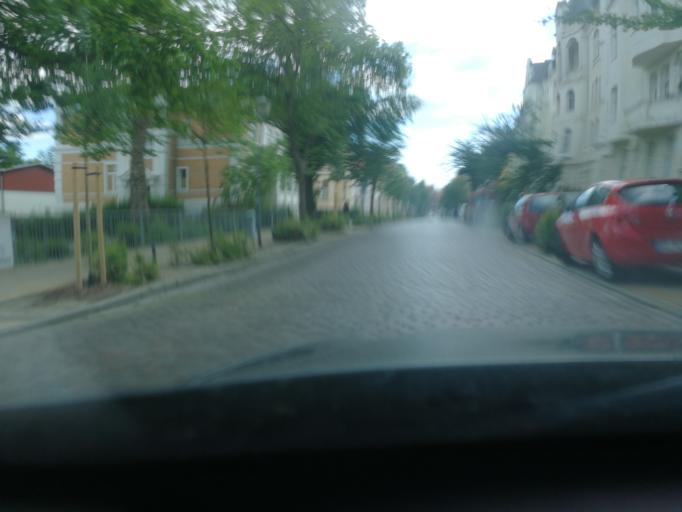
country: DE
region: Mecklenburg-Vorpommern
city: Stralsund
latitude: 54.3122
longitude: 13.0784
